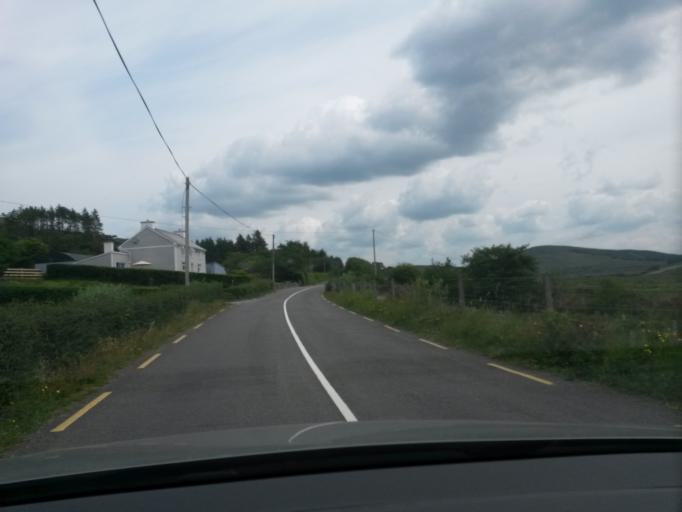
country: IE
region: Munster
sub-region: Ciarrai
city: Kenmare
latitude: 51.9136
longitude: -9.7025
